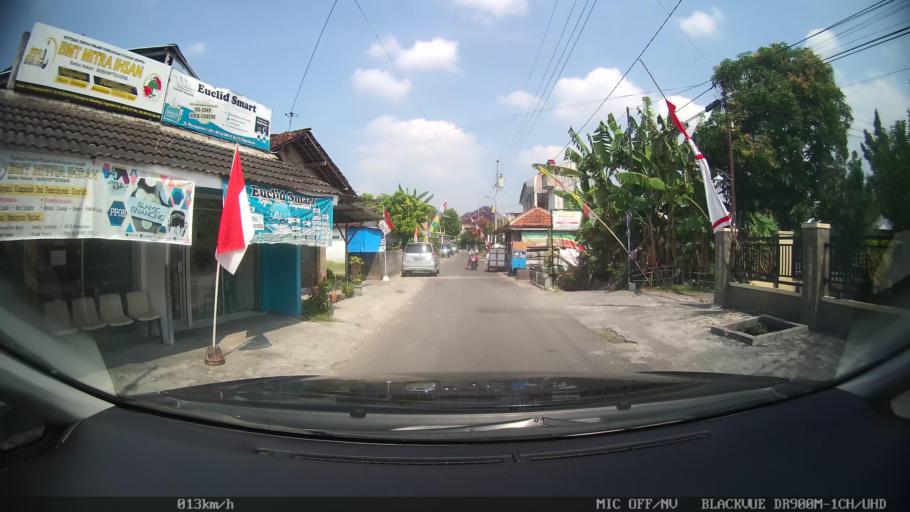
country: ID
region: Daerah Istimewa Yogyakarta
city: Yogyakarta
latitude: -7.8090
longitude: 110.3919
